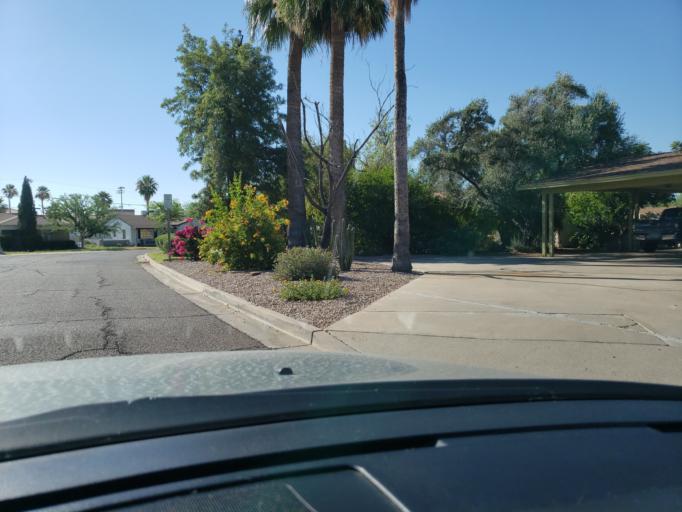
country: US
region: Arizona
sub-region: Maricopa County
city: Phoenix
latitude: 33.4795
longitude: -112.0611
